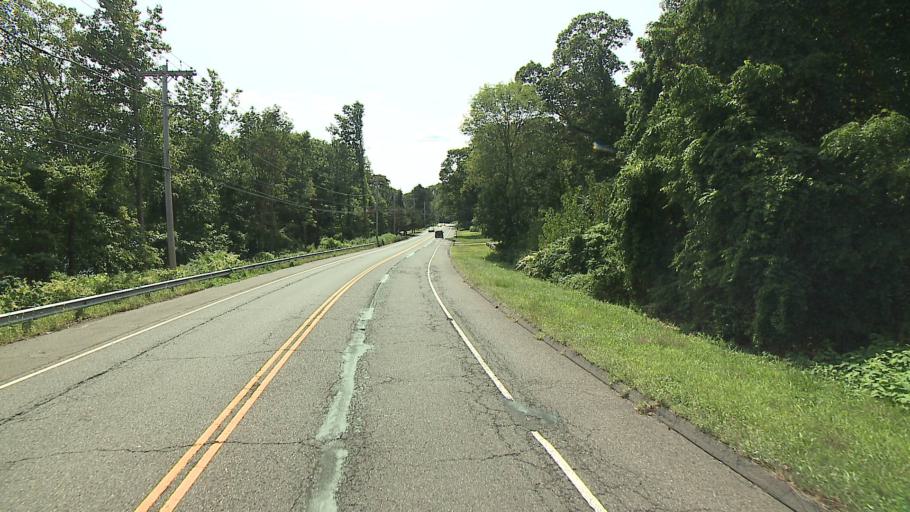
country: US
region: Connecticut
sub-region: Fairfield County
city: Shelton
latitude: 41.2746
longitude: -73.0891
